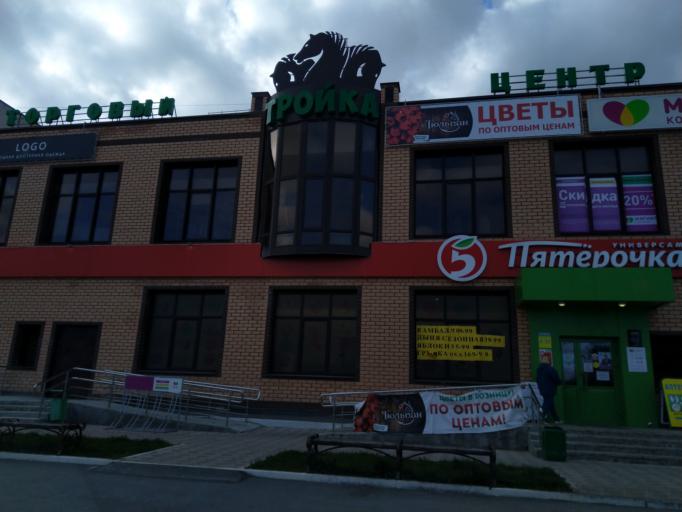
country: RU
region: Perm
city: Dobryanka
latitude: 58.4727
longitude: 56.4078
